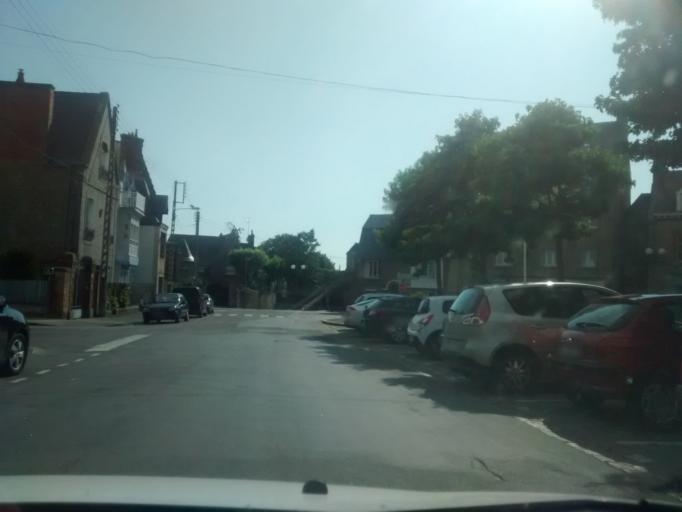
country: FR
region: Brittany
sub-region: Departement d'Ille-et-Vilaine
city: Saint-Malo
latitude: 48.6567
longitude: -1.9839
